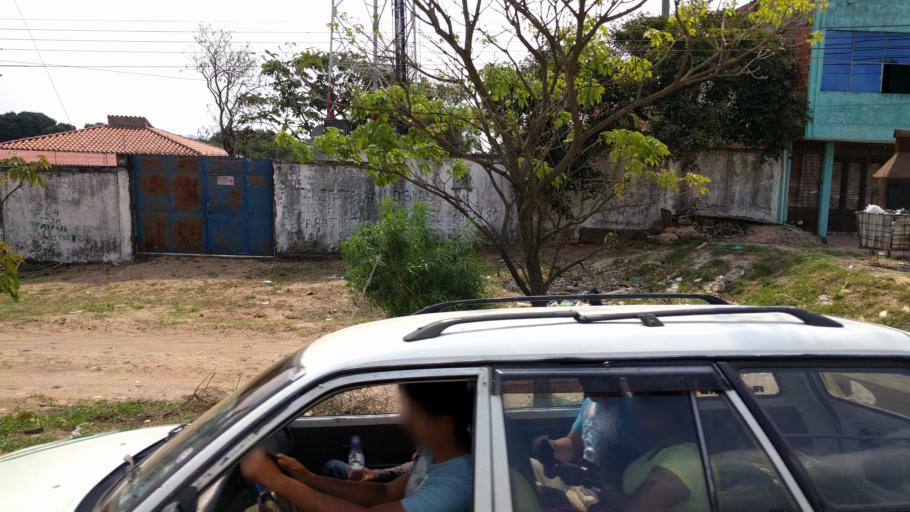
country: BO
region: Santa Cruz
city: Santa Rita
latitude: -17.8936
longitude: -63.3319
